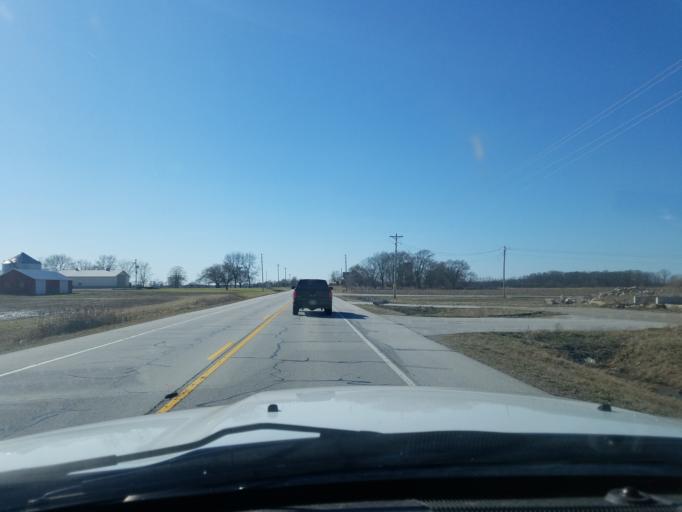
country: US
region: Indiana
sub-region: Shelby County
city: Shelbyville
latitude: 39.4959
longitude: -85.8932
